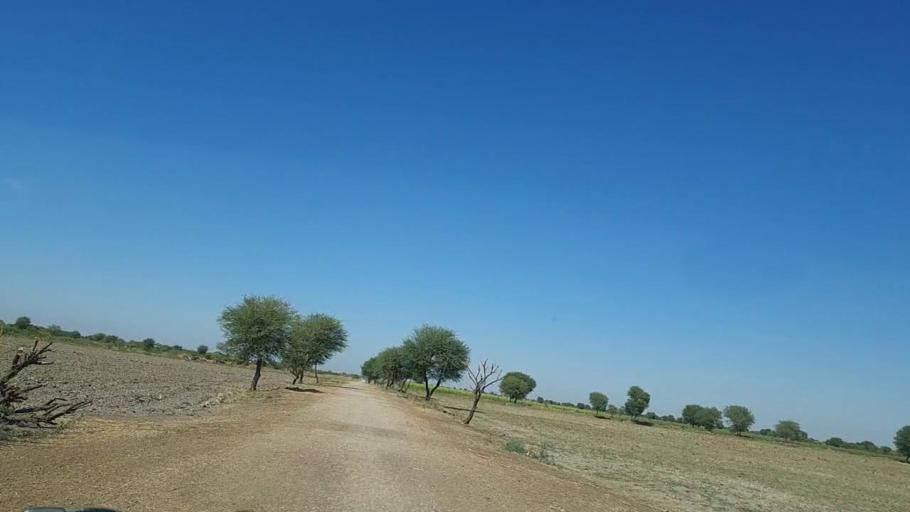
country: PK
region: Sindh
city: Pithoro
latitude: 25.5512
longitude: 69.4599
